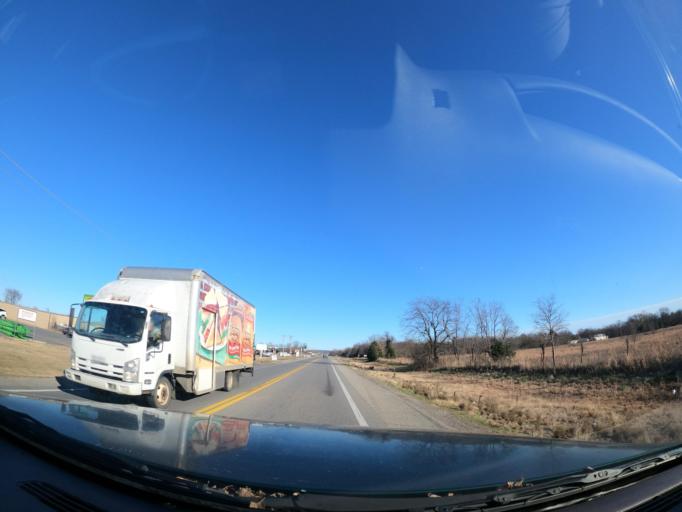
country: US
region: Oklahoma
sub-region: Pittsburg County
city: Longtown
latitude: 35.2392
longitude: -95.5191
